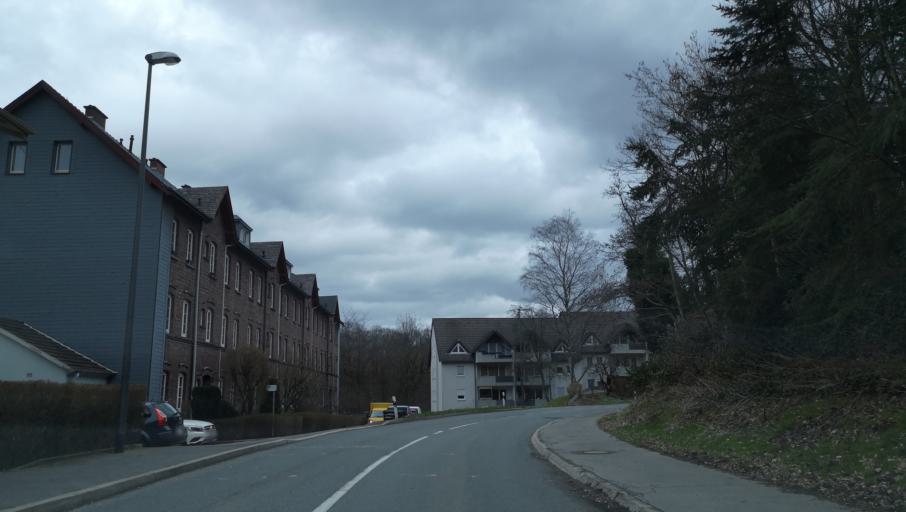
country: DE
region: North Rhine-Westphalia
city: Radevormwald
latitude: 51.2229
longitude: 7.3085
